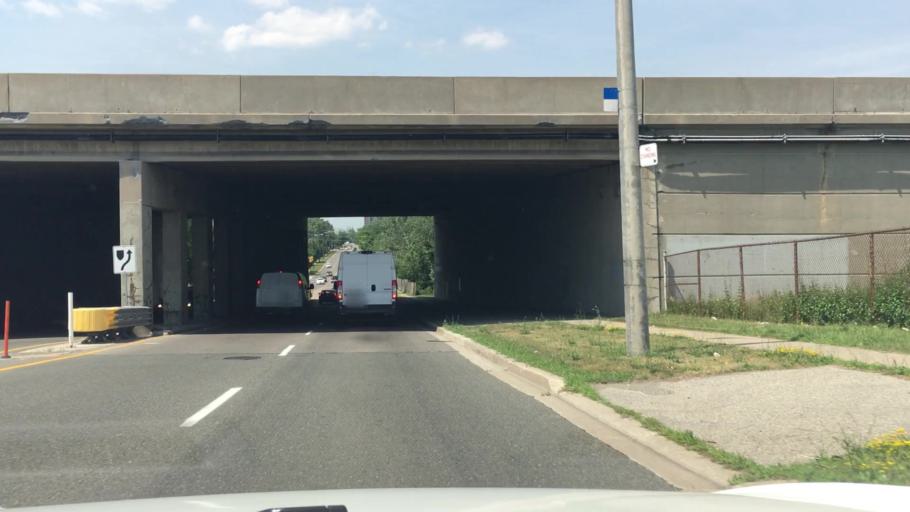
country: CA
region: Ontario
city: Scarborough
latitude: 43.7722
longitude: -79.2941
